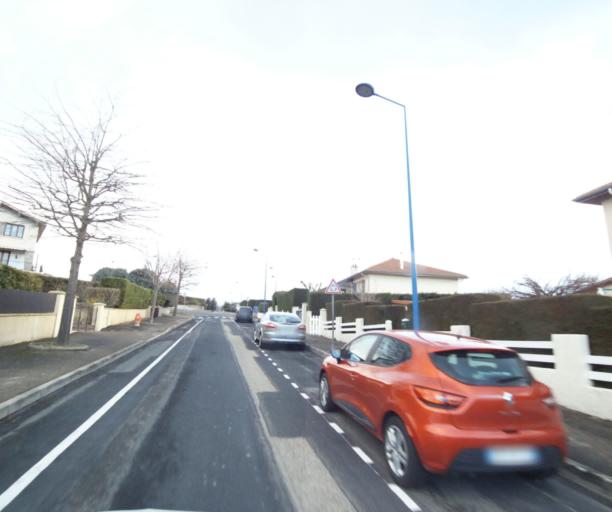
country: FR
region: Rhone-Alpes
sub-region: Departement de la Loire
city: La Talaudiere
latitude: 45.4841
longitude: 4.4317
